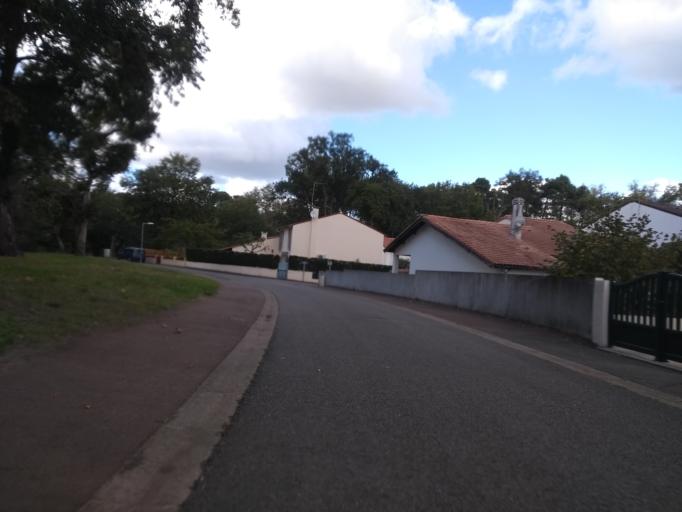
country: FR
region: Aquitaine
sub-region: Departement de la Gironde
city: Canejan
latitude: 44.7592
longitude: -0.6425
